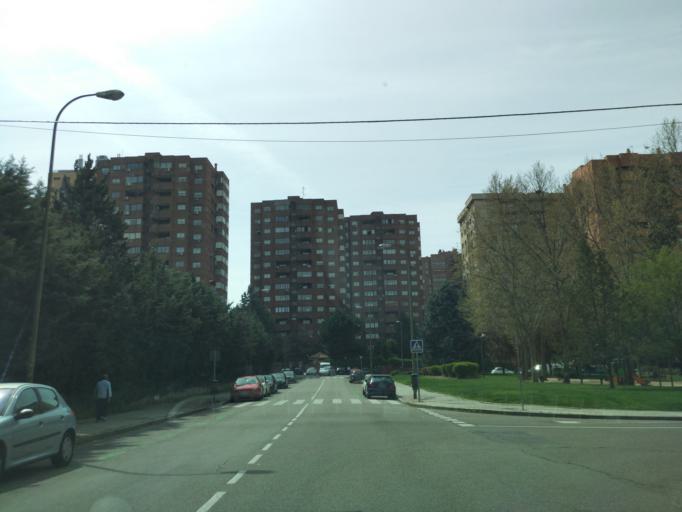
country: ES
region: Madrid
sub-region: Provincia de Madrid
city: Tetuan de las Victorias
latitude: 40.4788
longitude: -3.6968
